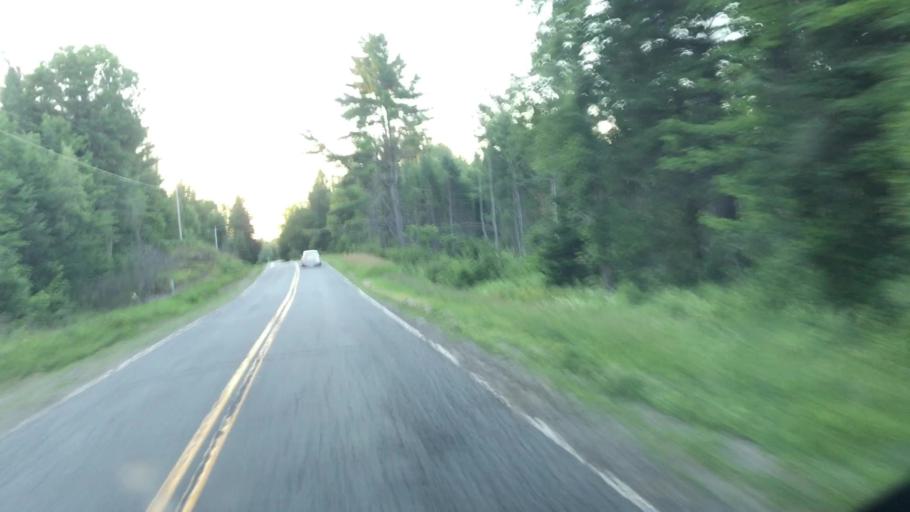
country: US
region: Maine
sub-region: Penobscot County
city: Medway
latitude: 45.6080
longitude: -68.2566
